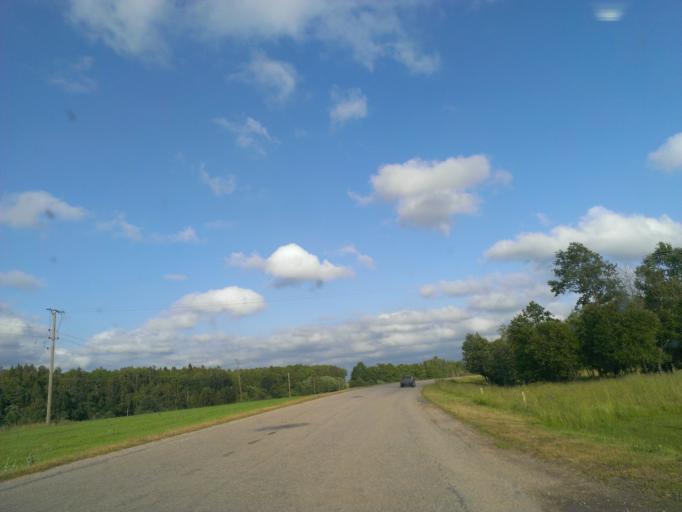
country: LV
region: Aizpute
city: Aizpute
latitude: 56.7552
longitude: 21.5569
